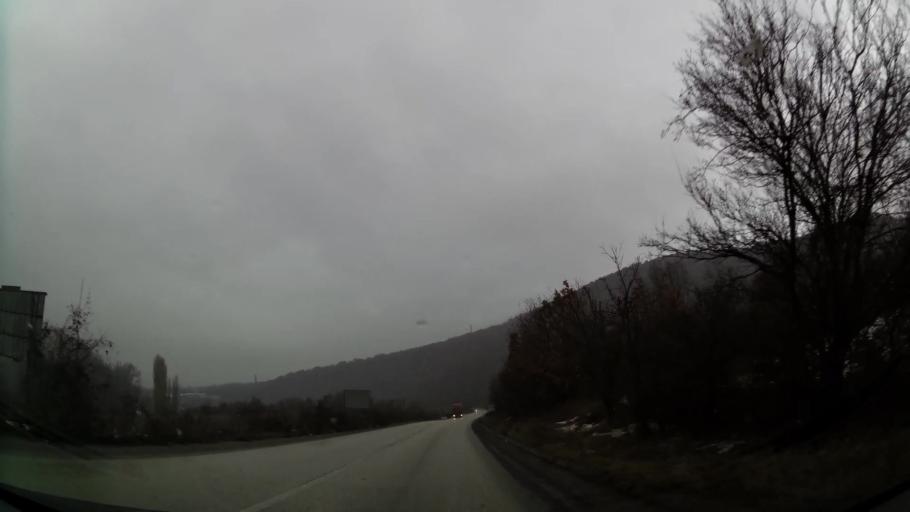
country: XK
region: Ferizaj
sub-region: Hani i Elezit
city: Hani i Elezit
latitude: 42.1281
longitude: 21.3119
